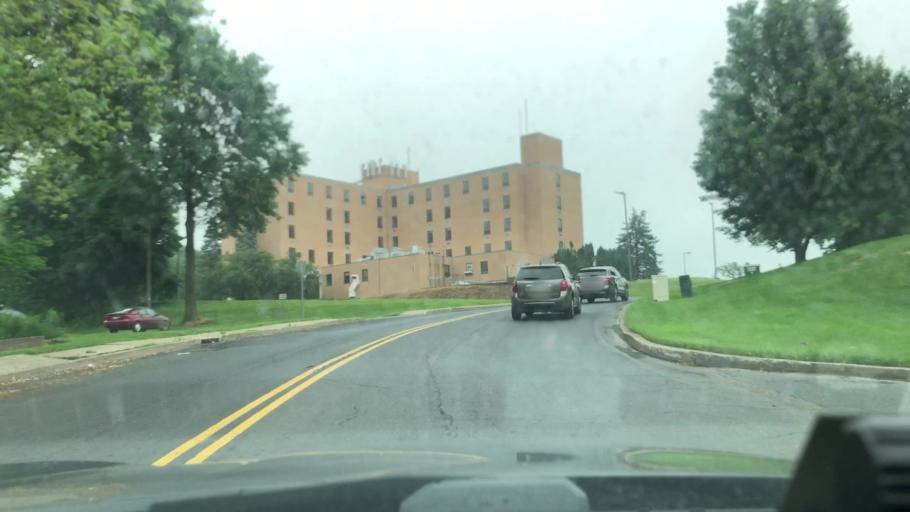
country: US
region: Pennsylvania
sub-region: Dauphin County
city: Progress
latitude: 40.2823
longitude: -76.8157
